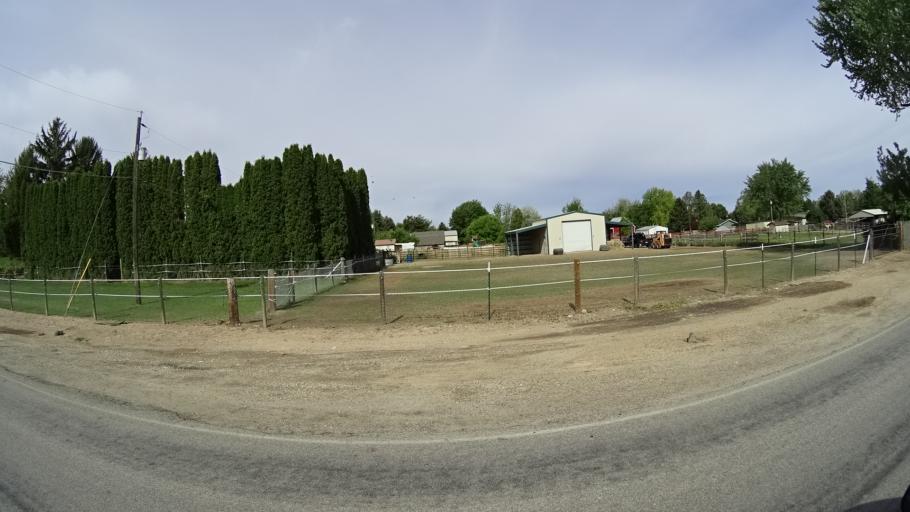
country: US
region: Idaho
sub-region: Ada County
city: Garden City
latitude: 43.5717
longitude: -116.3041
